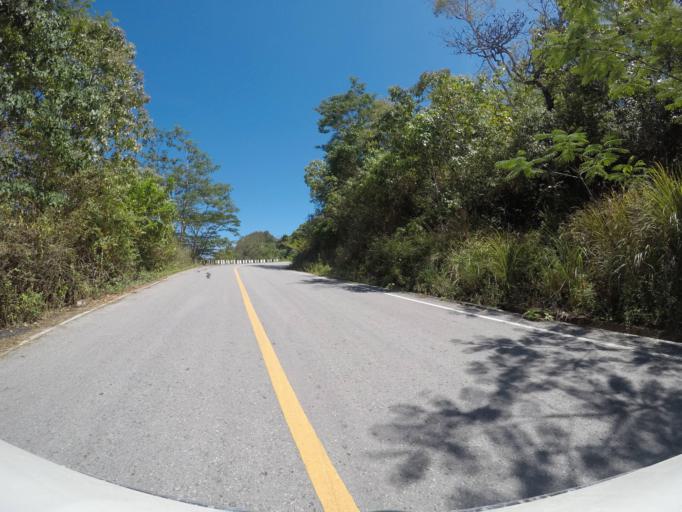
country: TL
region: Manatuto
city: Manatuto
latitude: -8.8182
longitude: 125.9755
